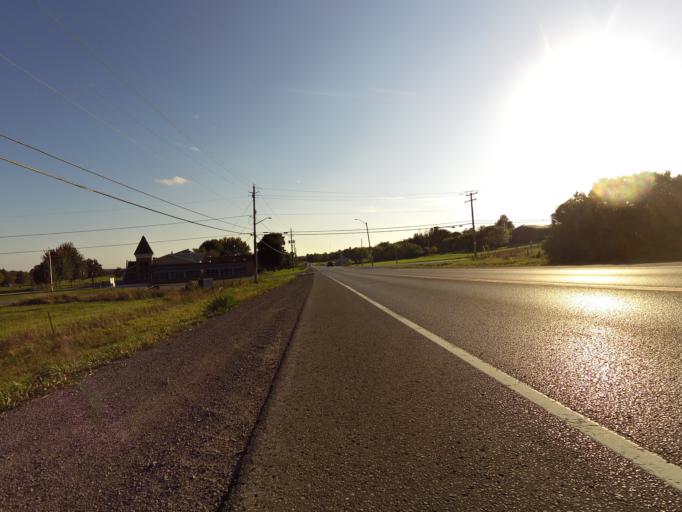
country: CA
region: Ontario
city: Kingston
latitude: 44.3220
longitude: -76.4613
